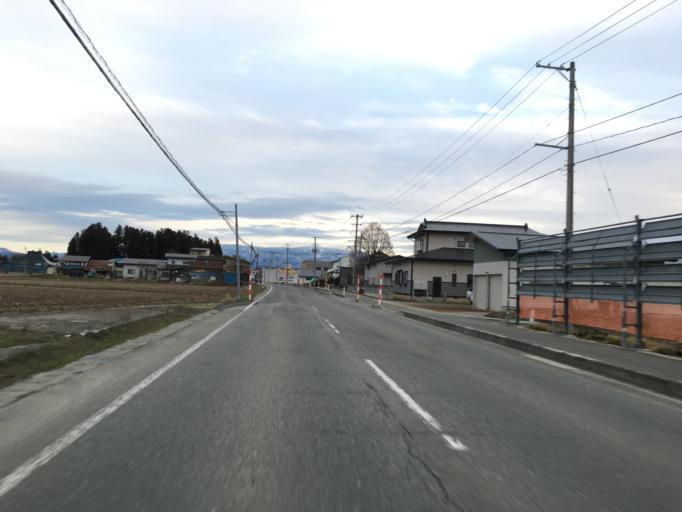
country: JP
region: Yamagata
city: Yonezawa
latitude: 37.9860
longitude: 140.0770
